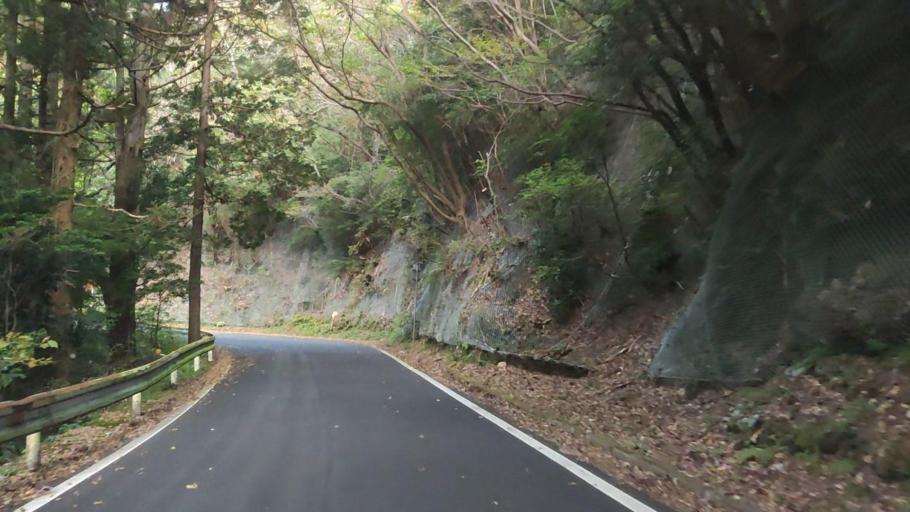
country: JP
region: Shizuoka
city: Ito
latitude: 34.9485
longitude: 139.0692
